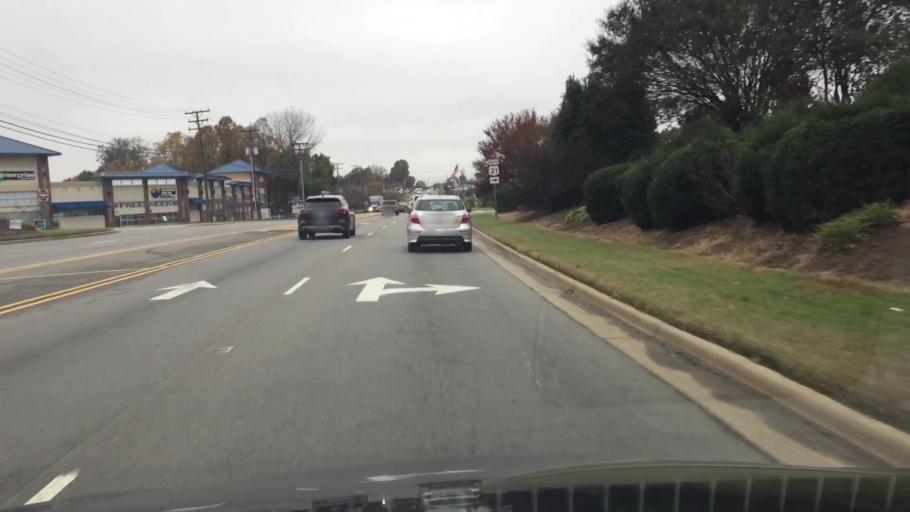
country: US
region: North Carolina
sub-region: Iredell County
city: Mooresville
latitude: 35.5892
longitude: -80.8383
